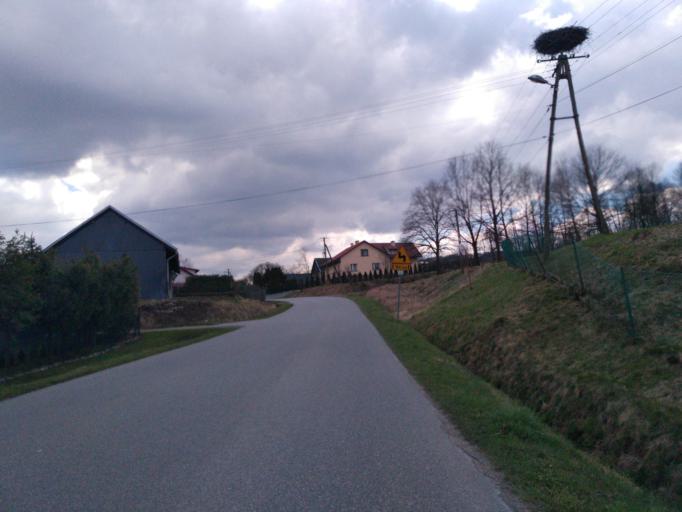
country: PL
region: Subcarpathian Voivodeship
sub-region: Powiat brzozowski
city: Dydnia
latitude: 49.6763
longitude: 22.1847
